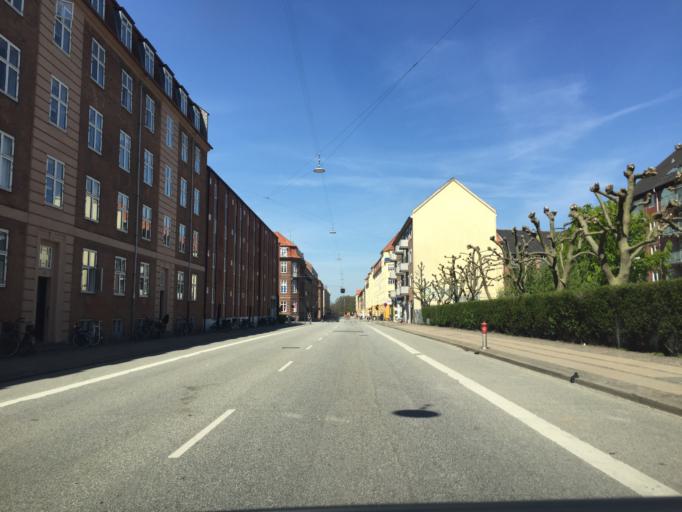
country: DK
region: Capital Region
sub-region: Kobenhavn
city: Copenhagen
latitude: 55.7103
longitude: 12.5696
